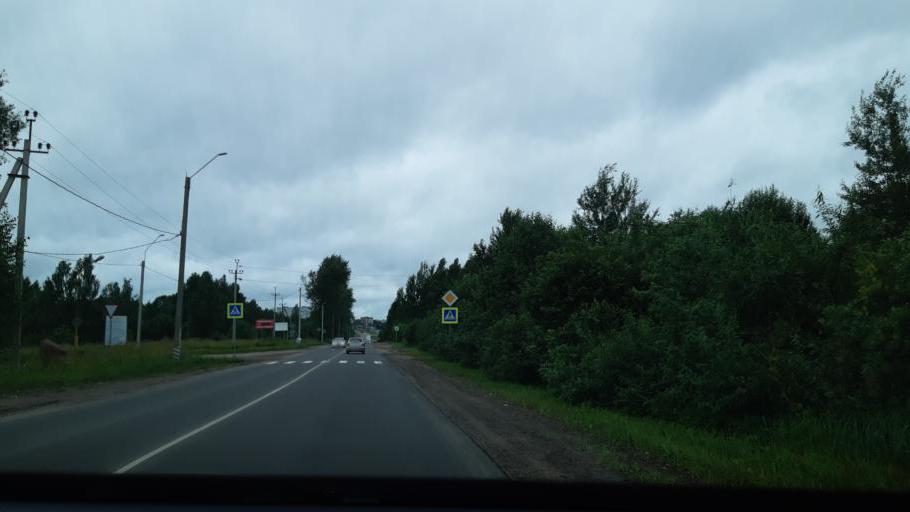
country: RU
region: Smolensk
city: Desnogorsk
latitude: 54.1353
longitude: 33.2775
